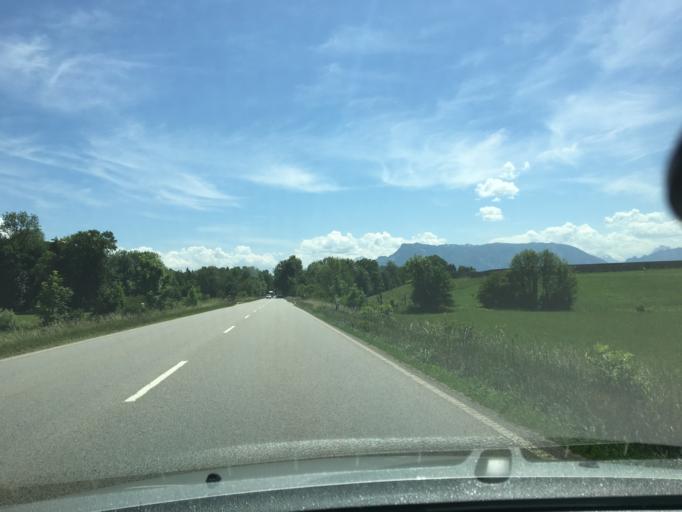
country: DE
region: Bavaria
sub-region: Upper Bavaria
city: Freilassing
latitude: 47.8663
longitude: 12.9782
